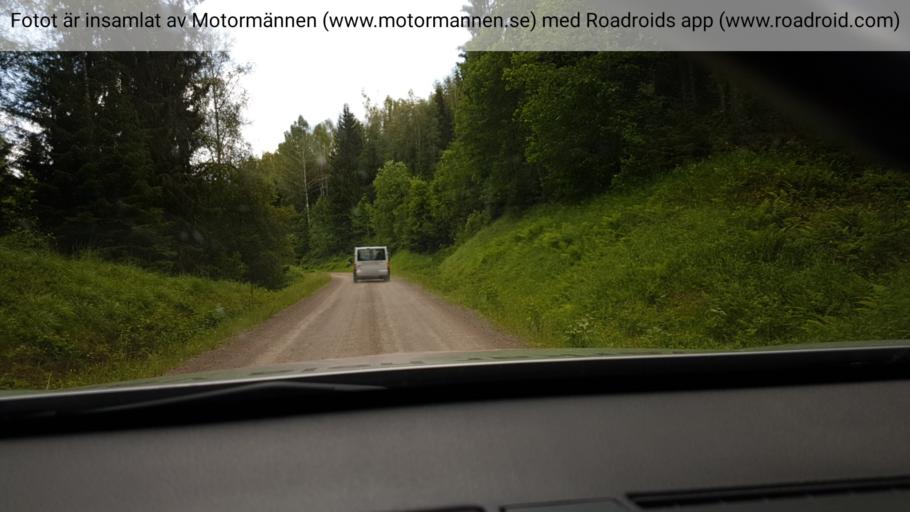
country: SE
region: Vaermland
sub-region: Hagfors Kommun
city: Ekshaerad
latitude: 60.3377
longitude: 13.3411
